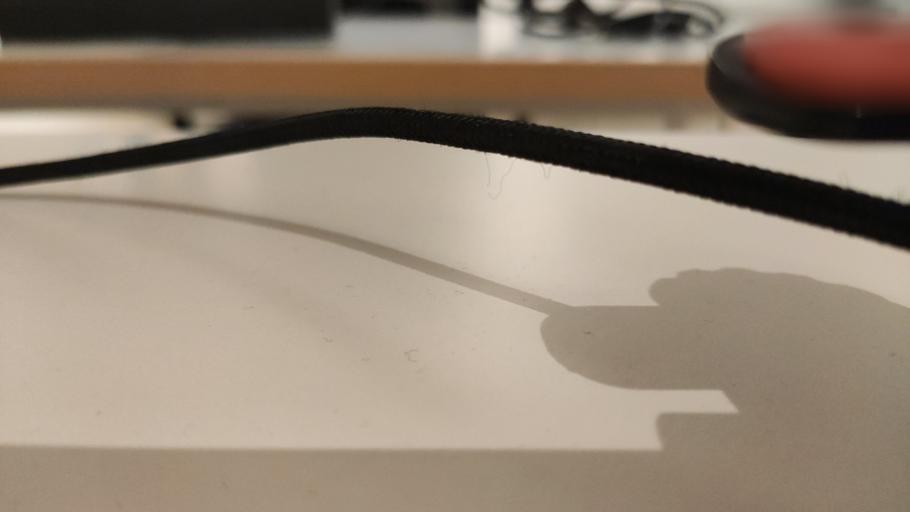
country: RU
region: Moskovskaya
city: Dorokhovo
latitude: 55.4501
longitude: 36.3523
